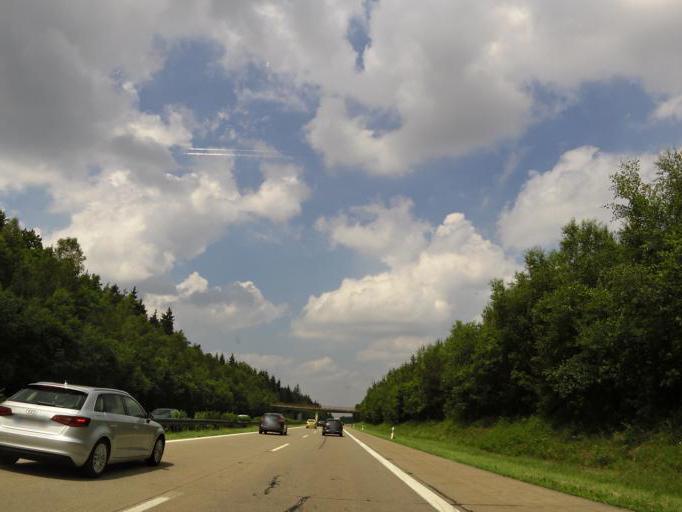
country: DE
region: Baden-Wuerttemberg
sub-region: Regierungsbezirk Stuttgart
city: Ellenberg
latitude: 49.0378
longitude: 10.1853
